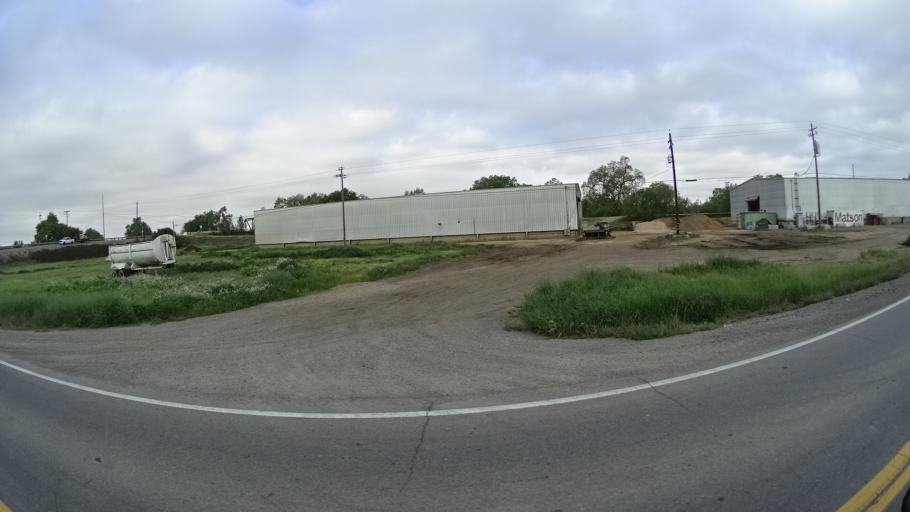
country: US
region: California
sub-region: Glenn County
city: Willows
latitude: 39.4586
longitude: -121.9922
